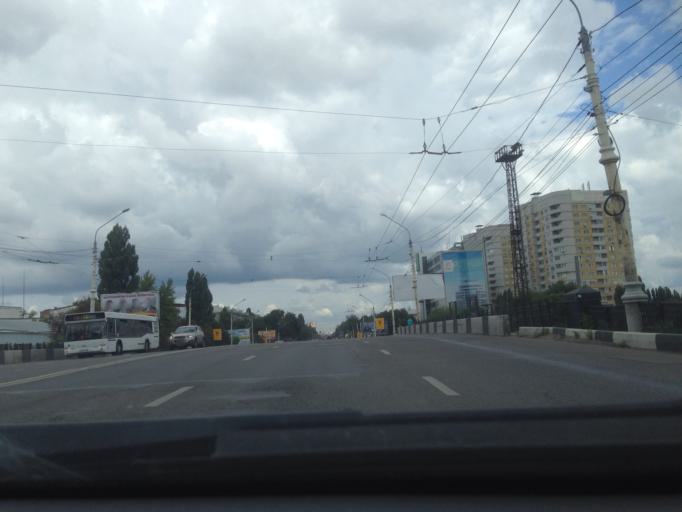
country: RU
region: Voronezj
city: Voronezh
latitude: 51.6762
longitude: 39.1852
